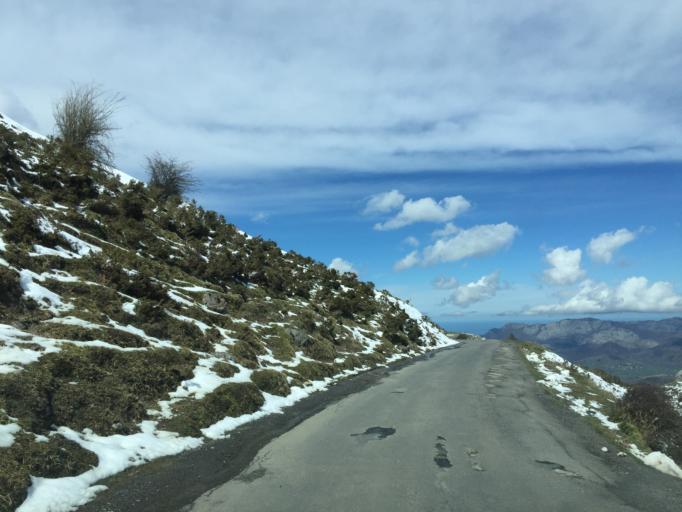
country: ES
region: Asturias
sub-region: Province of Asturias
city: Amieva
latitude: 43.2742
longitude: -4.9825
